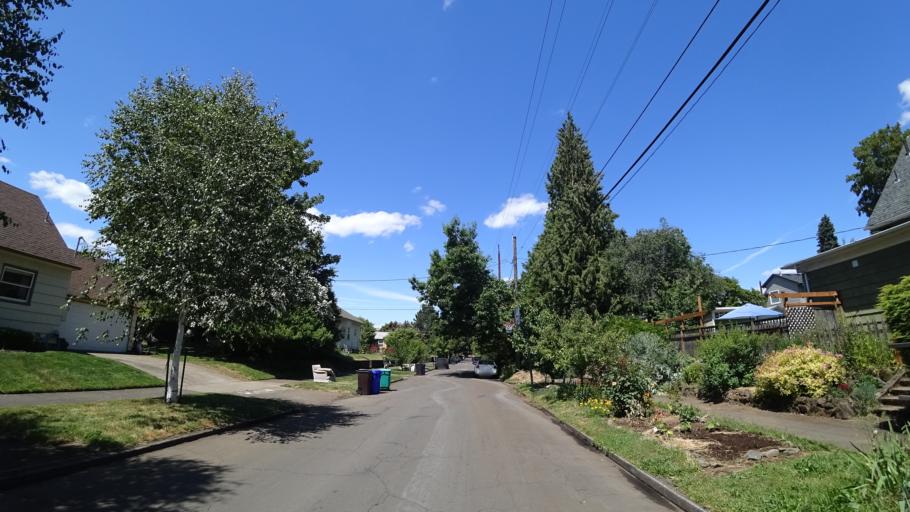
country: US
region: Oregon
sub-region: Multnomah County
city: Portland
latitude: 45.5642
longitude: -122.6848
